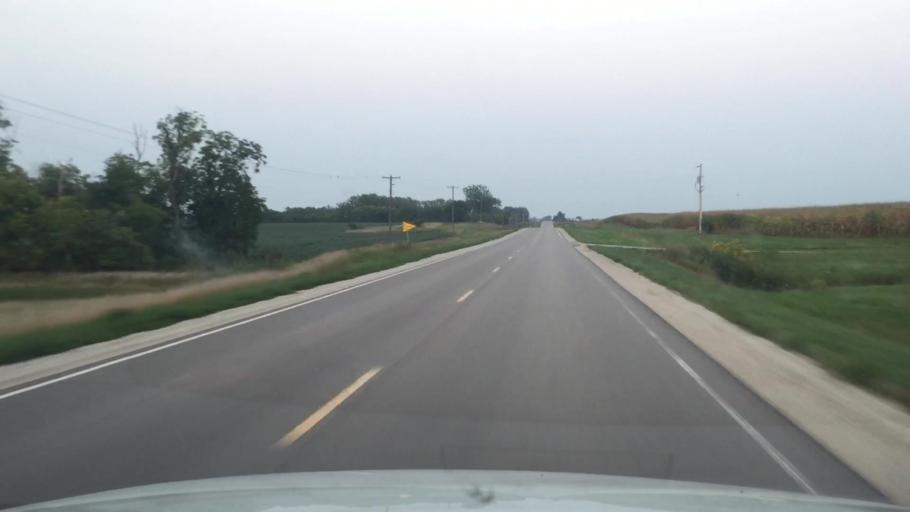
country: US
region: Iowa
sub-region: Warren County
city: Indianola
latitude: 41.1826
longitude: -93.4895
